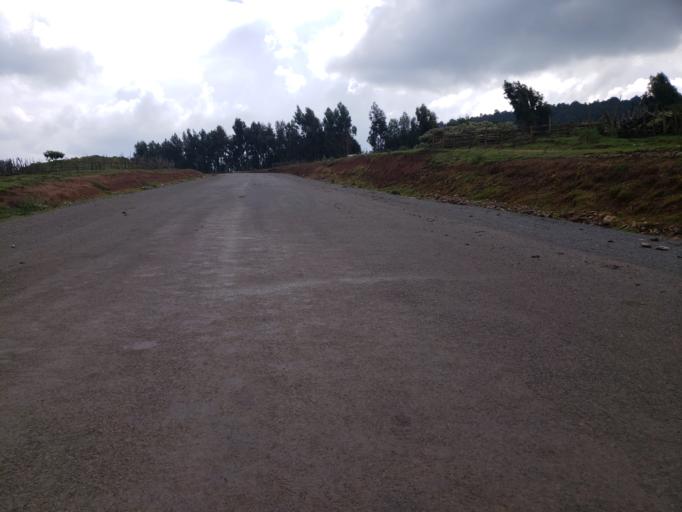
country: ET
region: Oromiya
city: Dodola
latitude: 6.8844
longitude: 39.3869
